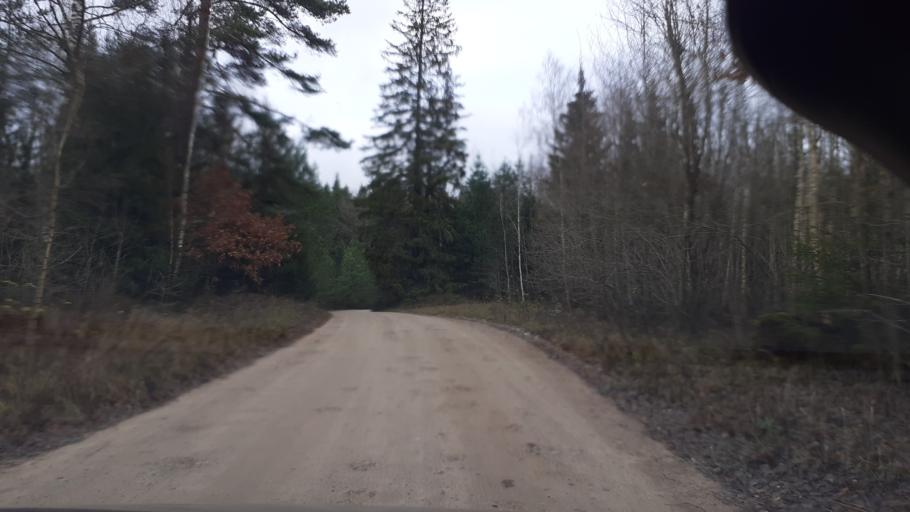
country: LV
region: Kuldigas Rajons
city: Kuldiga
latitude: 57.0318
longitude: 21.8728
